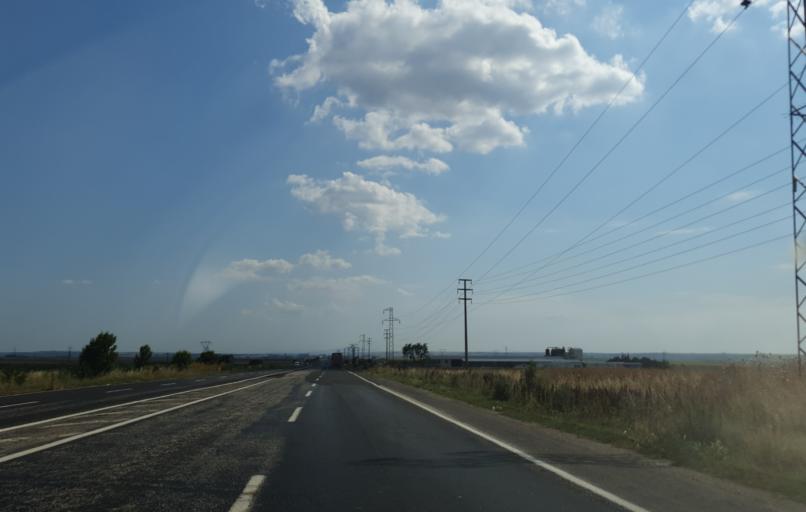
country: TR
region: Kirklareli
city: Buyukkaristiran
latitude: 41.2487
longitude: 27.5413
